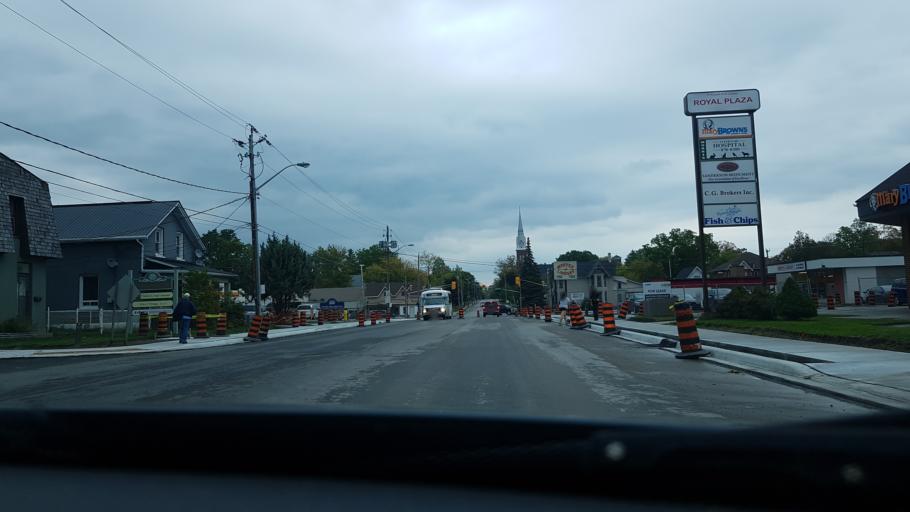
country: CA
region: Ontario
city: Omemee
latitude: 44.3539
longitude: -78.7357
